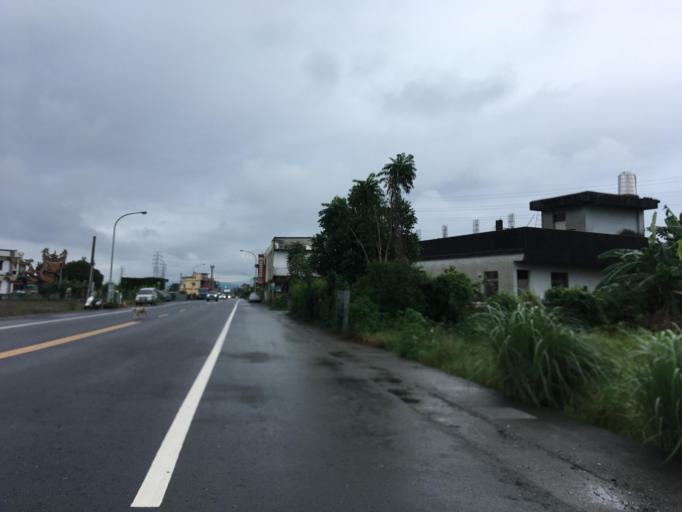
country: TW
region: Taiwan
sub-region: Yilan
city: Yilan
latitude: 24.6624
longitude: 121.7524
